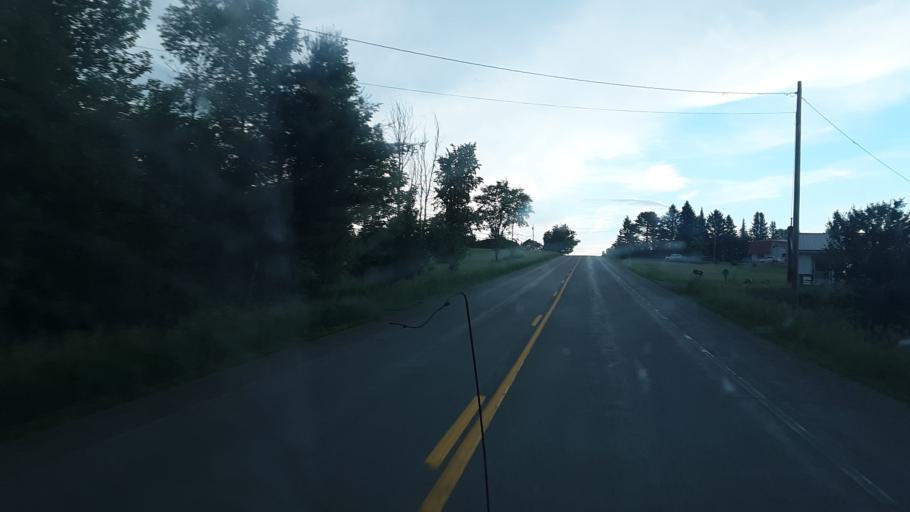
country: US
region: Maine
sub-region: Aroostook County
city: Hodgdon
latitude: 45.7777
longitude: -67.8630
